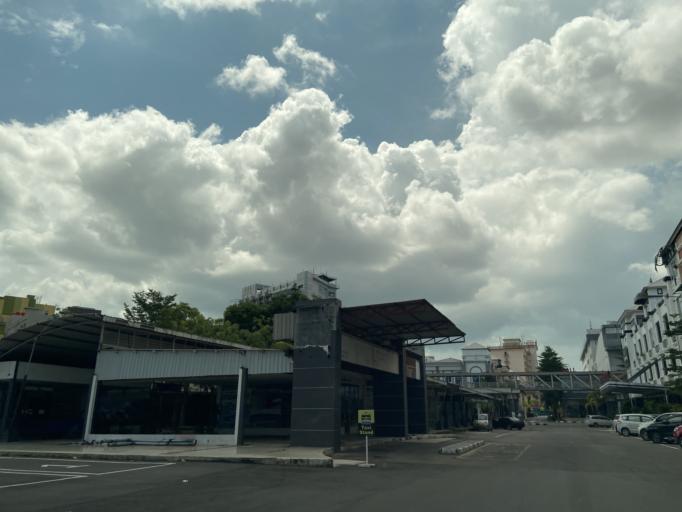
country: SG
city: Singapore
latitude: 1.1531
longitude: 103.9984
